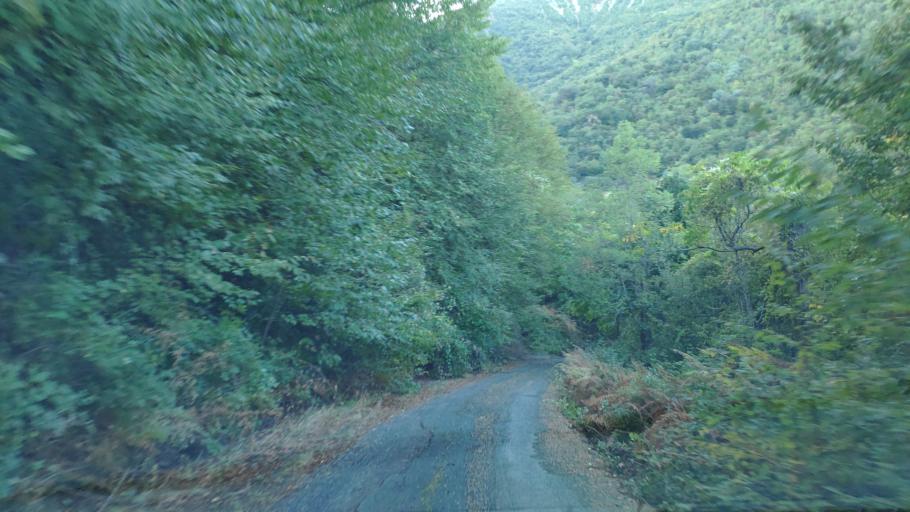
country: GR
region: Peloponnese
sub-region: Nomos Arkadias
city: Dimitsana
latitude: 37.5652
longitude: 22.0417
